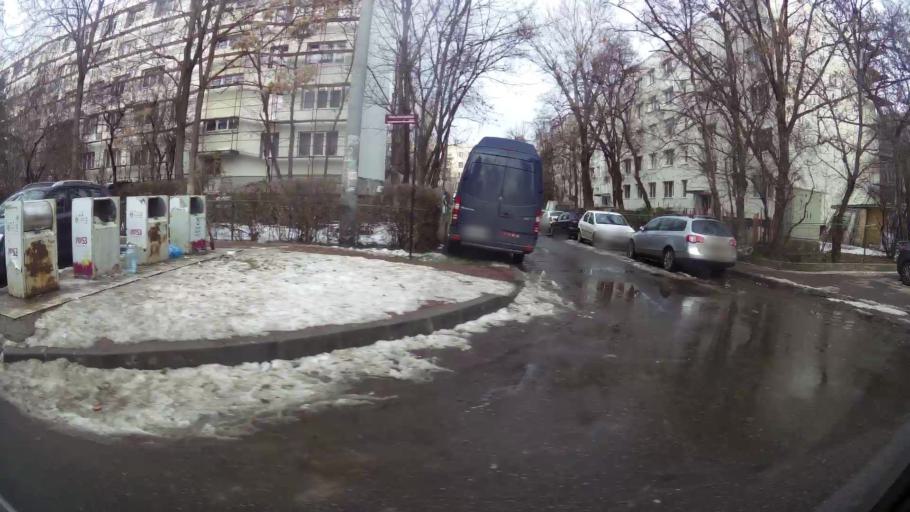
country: RO
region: Ilfov
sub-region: Comuna Popesti-Leordeni
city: Popesti-Leordeni
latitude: 44.4064
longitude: 26.1746
